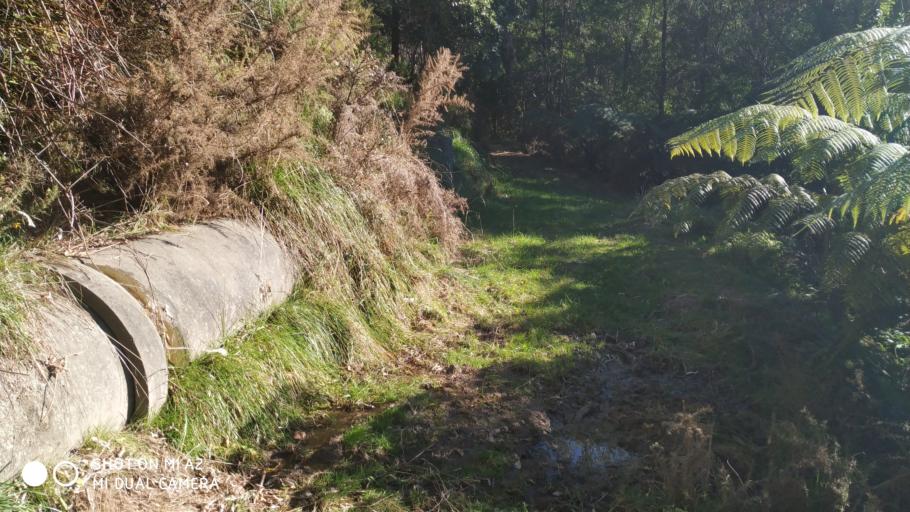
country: NZ
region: Nelson
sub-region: Nelson City
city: Nelson
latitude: -41.2940
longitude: 173.3217
